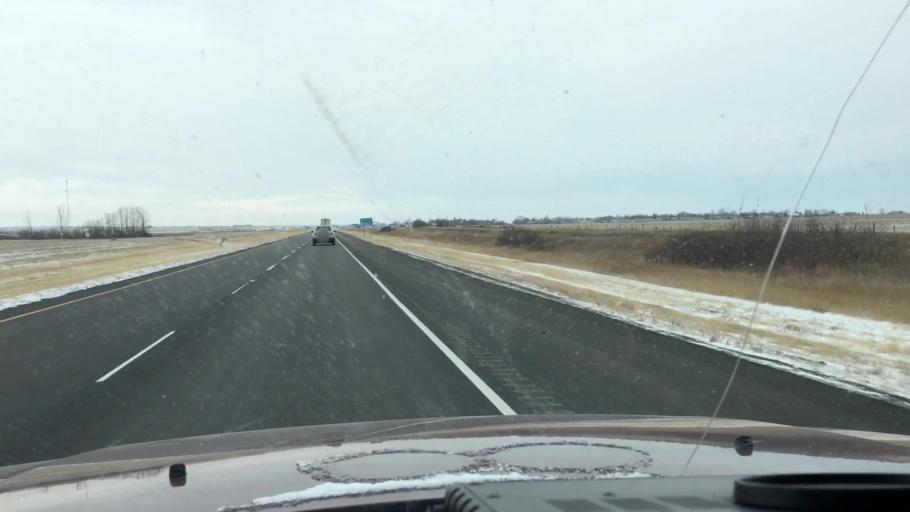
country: CA
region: Saskatchewan
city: Saskatoon
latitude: 51.8283
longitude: -106.5014
